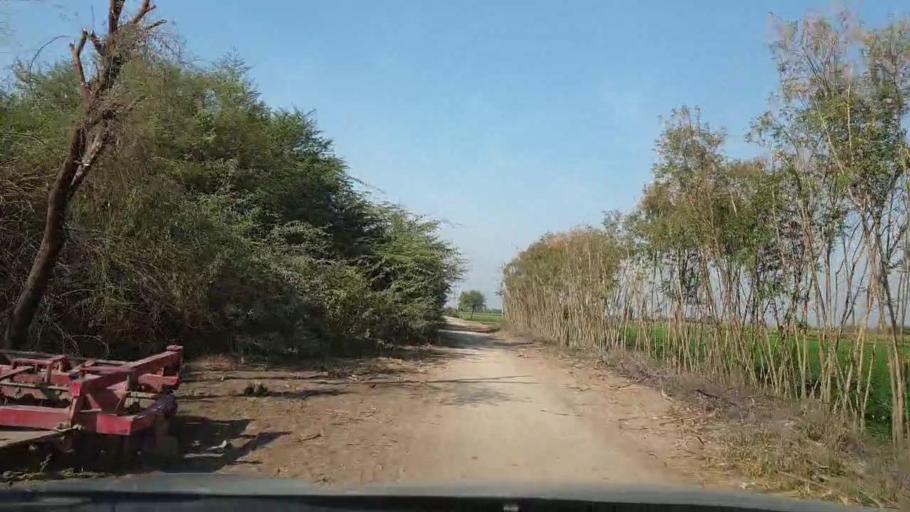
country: PK
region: Sindh
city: Berani
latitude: 25.7256
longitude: 68.7617
